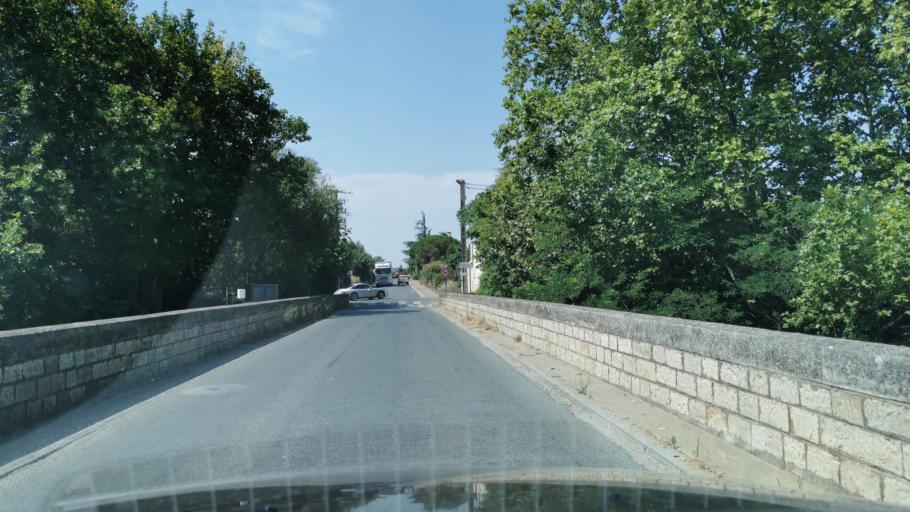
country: FR
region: Languedoc-Roussillon
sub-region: Departement de l'Aude
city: Argeliers
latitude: 43.2843
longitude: 2.9007
